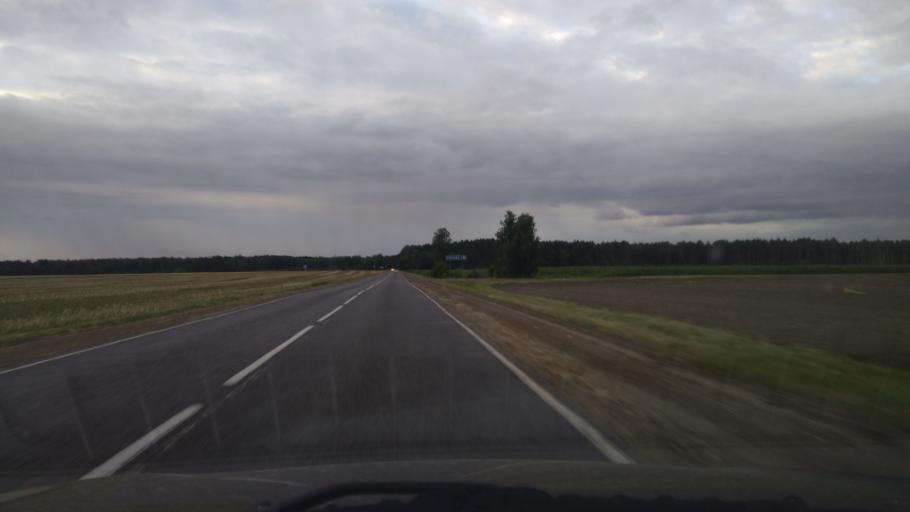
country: BY
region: Brest
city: Byaroza
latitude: 52.3978
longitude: 25.0058
